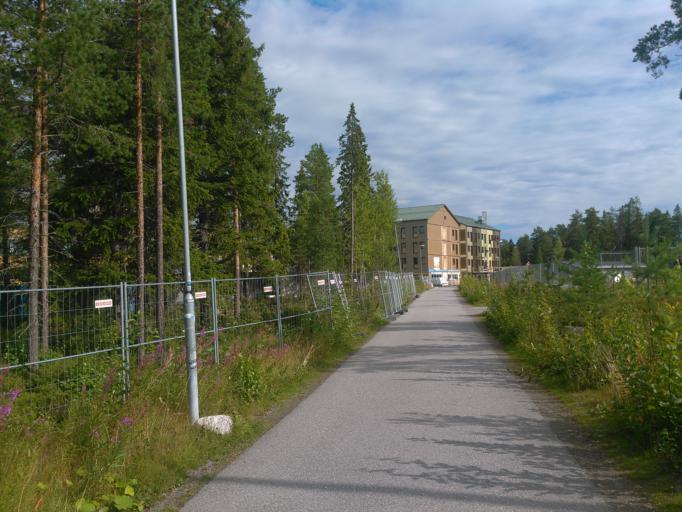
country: SE
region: Vaesterbotten
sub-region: Umea Kommun
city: Umea
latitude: 63.8209
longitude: 20.3186
